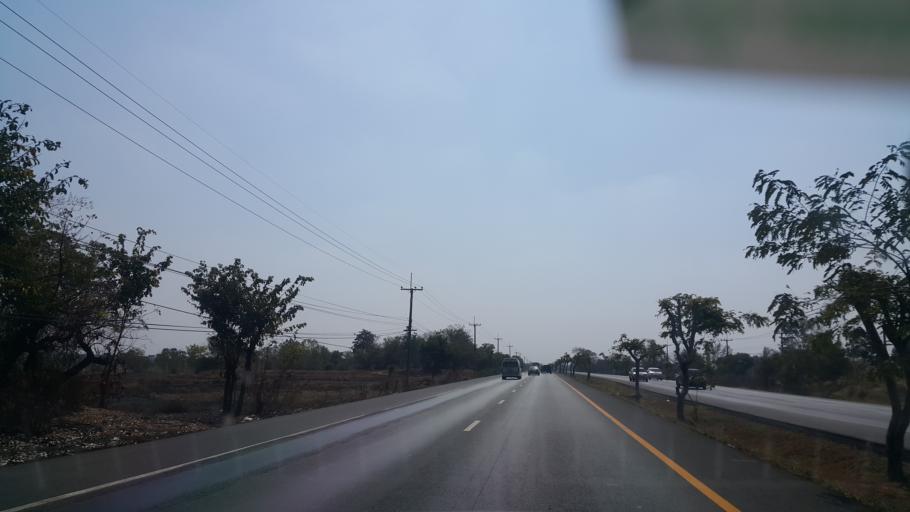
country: TH
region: Nakhon Ratchasima
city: Non Daeng
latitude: 15.4295
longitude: 102.4880
